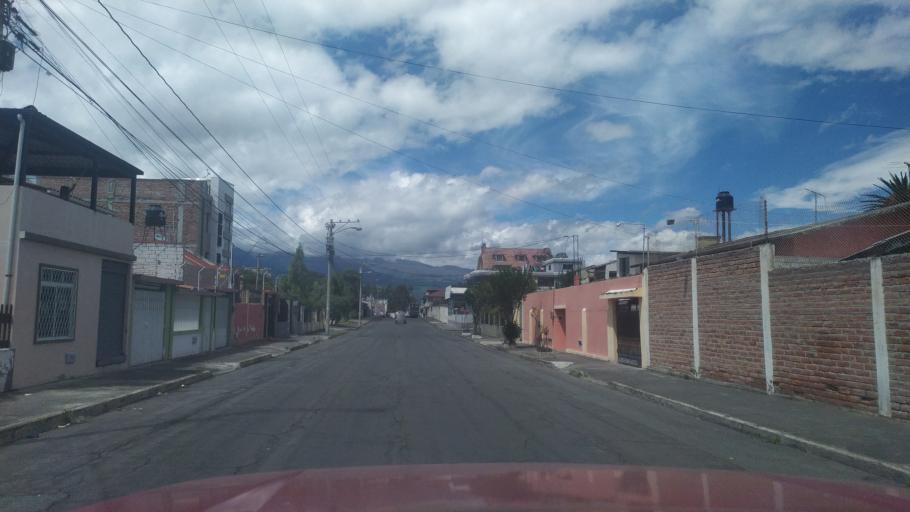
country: EC
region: Chimborazo
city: Riobamba
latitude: -1.6738
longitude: -78.6398
